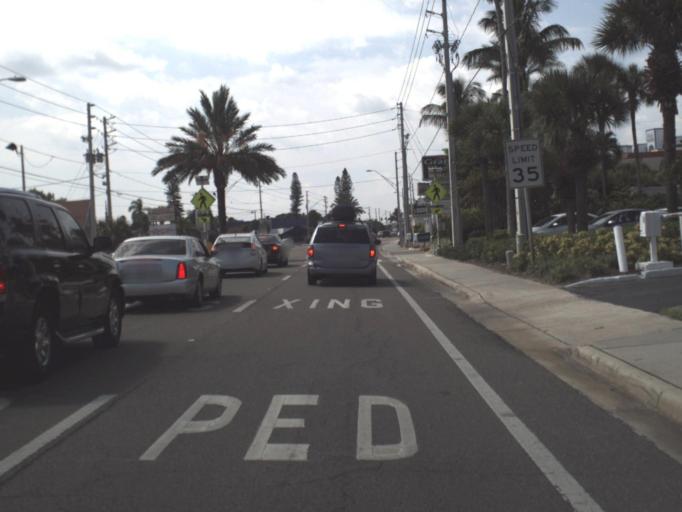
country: US
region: Florida
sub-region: Pinellas County
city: Saint Pete Beach
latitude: 27.7271
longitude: -82.7422
